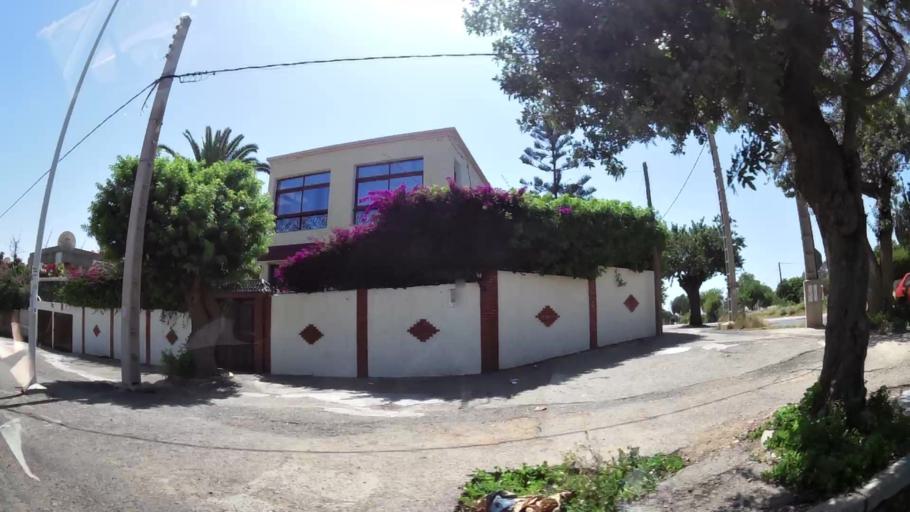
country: MA
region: Souss-Massa-Draa
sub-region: Agadir-Ida-ou-Tnan
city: Agadir
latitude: 30.4316
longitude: -9.5939
